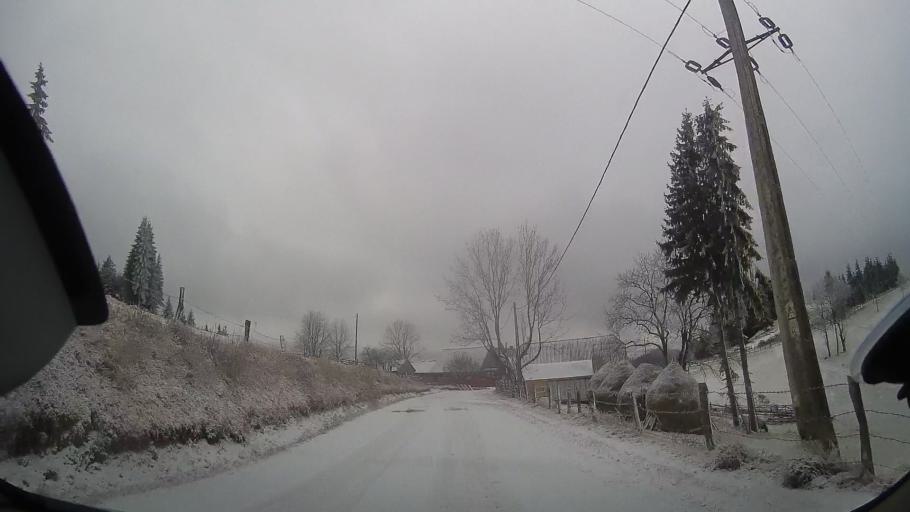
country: RO
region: Cluj
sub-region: Comuna Marisel
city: Marisel
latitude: 46.6578
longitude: 23.1395
